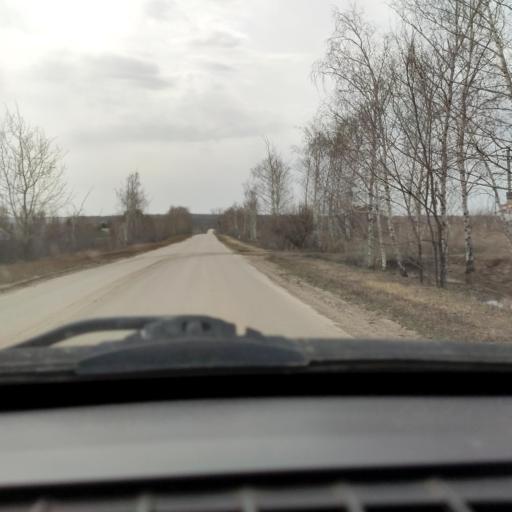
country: RU
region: Samara
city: Dubovyy Umet
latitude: 53.0451
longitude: 50.1829
